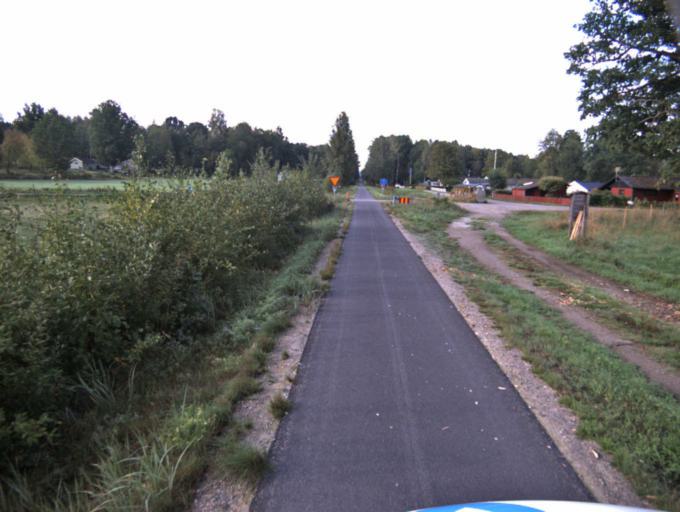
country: SE
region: Vaestra Goetaland
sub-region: Ulricehamns Kommun
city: Ulricehamn
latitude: 57.7209
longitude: 13.4010
